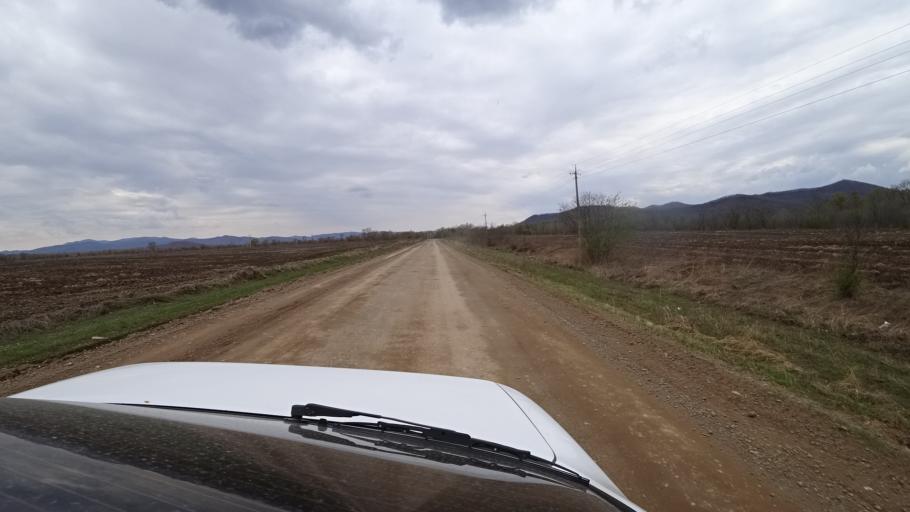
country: RU
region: Primorskiy
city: Novopokrovka
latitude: 45.5567
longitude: 134.3550
